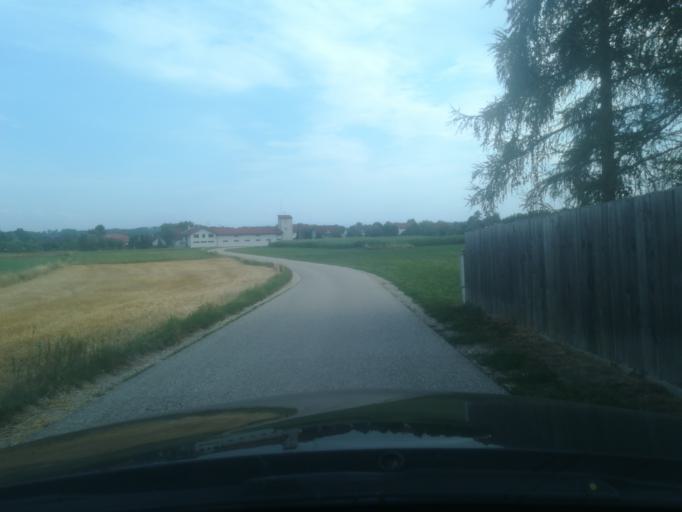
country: AT
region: Upper Austria
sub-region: Wels-Land
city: Marchtrenk
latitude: 48.1917
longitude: 14.1295
